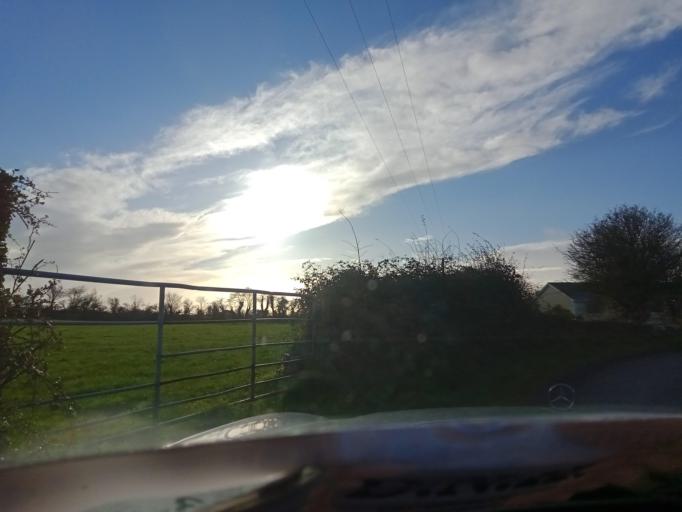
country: IE
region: Leinster
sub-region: Kilkenny
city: Mooncoin
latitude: 52.2782
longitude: -7.2123
